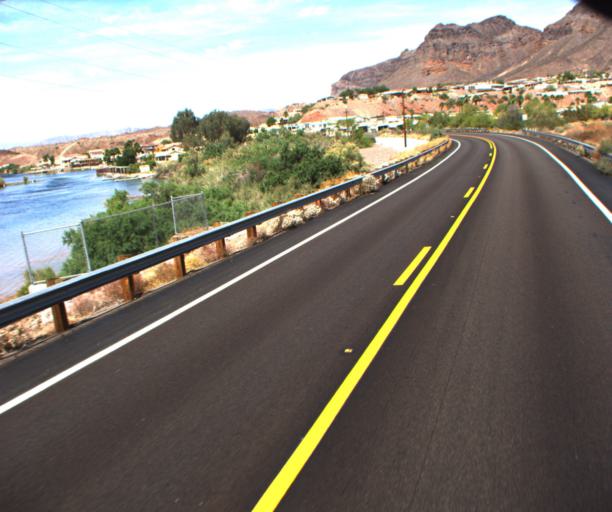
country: US
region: Arizona
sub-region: La Paz County
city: Cienega Springs
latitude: 34.2579
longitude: -114.1306
